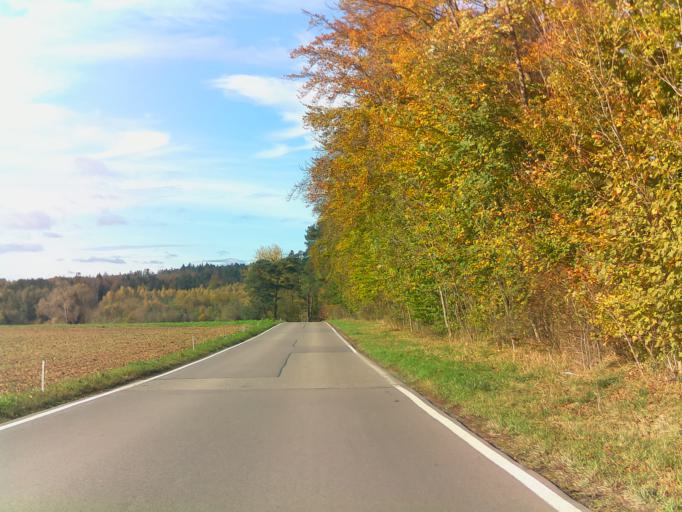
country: DE
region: Baden-Wuerttemberg
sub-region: Karlsruhe Region
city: Tiefenbronn
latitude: 48.8396
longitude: 8.8124
